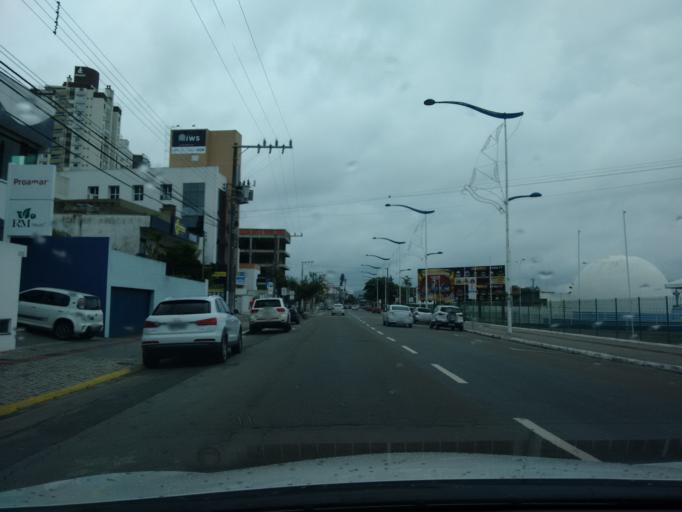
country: BR
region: Santa Catarina
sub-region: Itajai
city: Itajai
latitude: -26.9095
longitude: -48.6541
